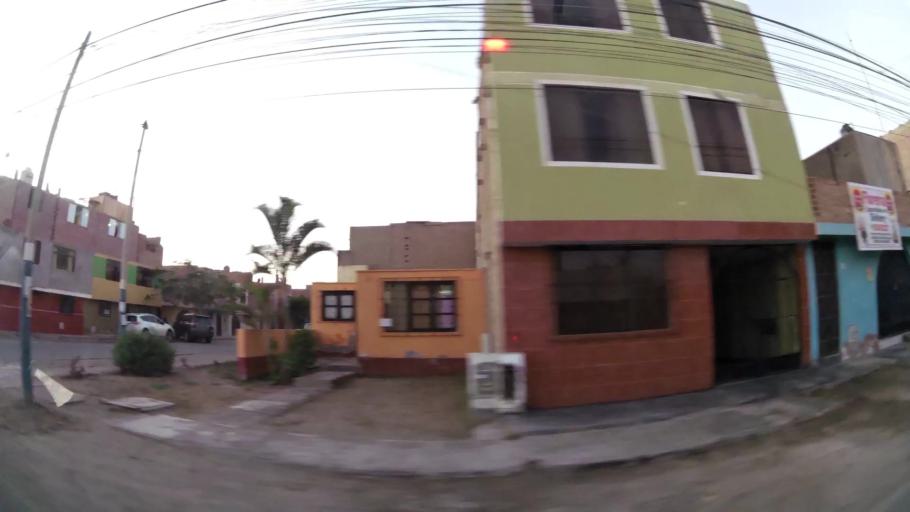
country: PE
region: Ica
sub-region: Provincia de Pisco
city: Pisco
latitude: -13.7070
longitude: -76.2061
